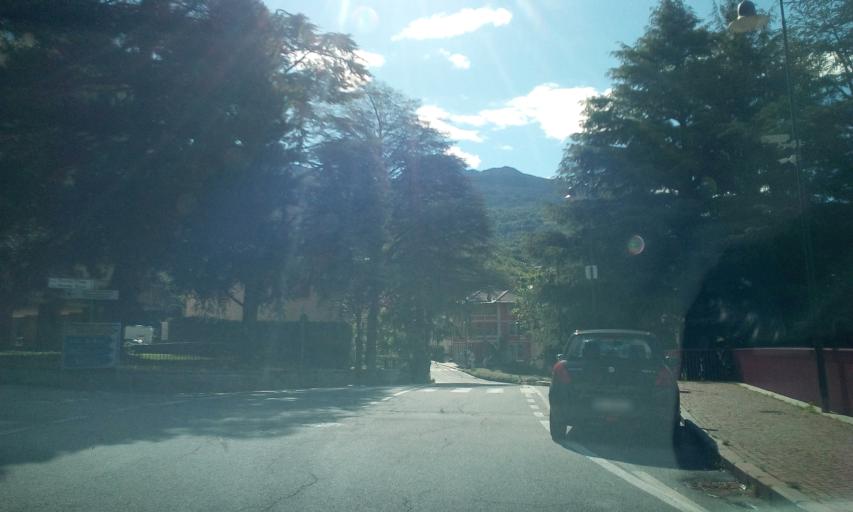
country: IT
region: Aosta Valley
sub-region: Valle d'Aosta
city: Saint-Vincent
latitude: 45.7531
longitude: 7.6460
